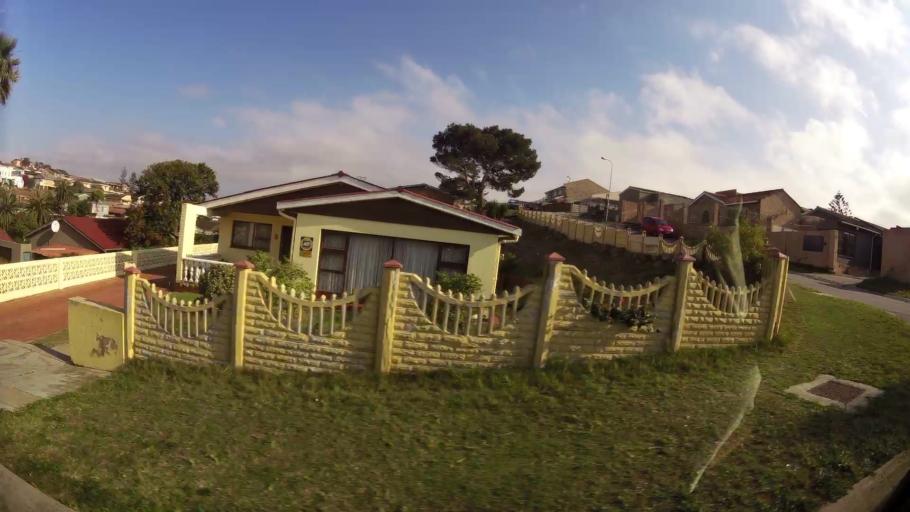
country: ZA
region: Eastern Cape
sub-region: Nelson Mandela Bay Metropolitan Municipality
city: Port Elizabeth
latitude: -33.9268
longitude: 25.5453
